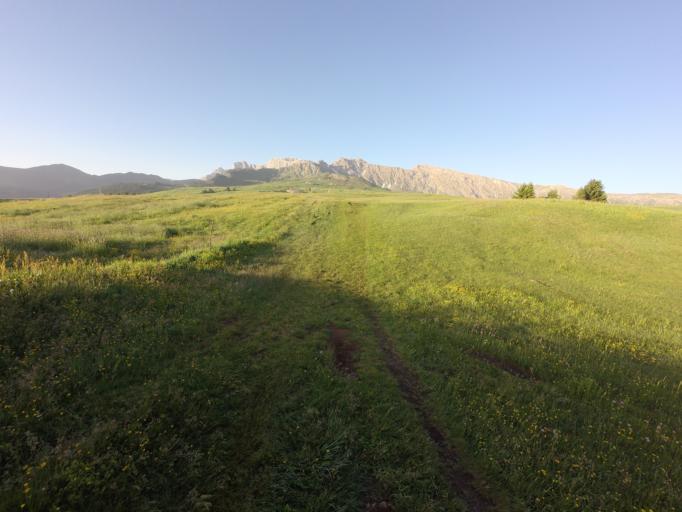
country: IT
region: Trentino-Alto Adige
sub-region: Bolzano
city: Ortisei
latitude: 46.5367
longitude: 11.6374
